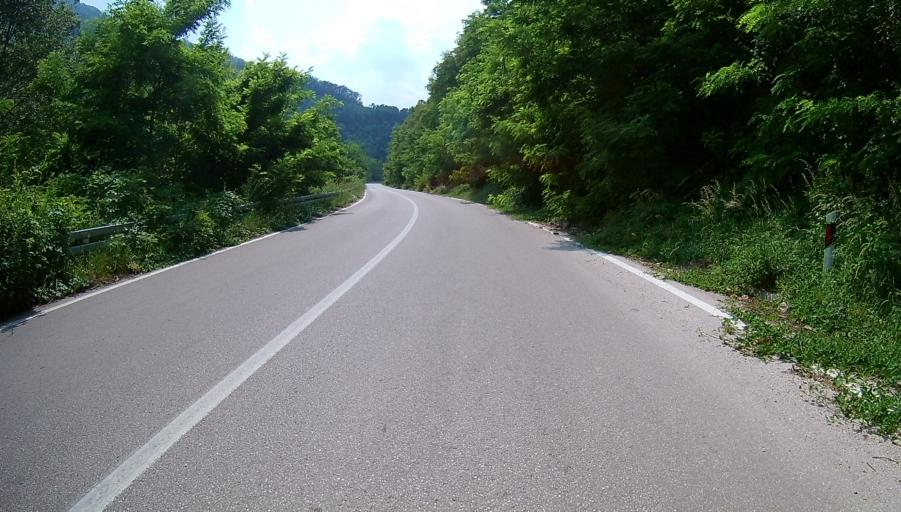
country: RS
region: Central Serbia
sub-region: Nisavski Okrug
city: Gadzin Han
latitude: 43.1721
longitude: 22.0675
